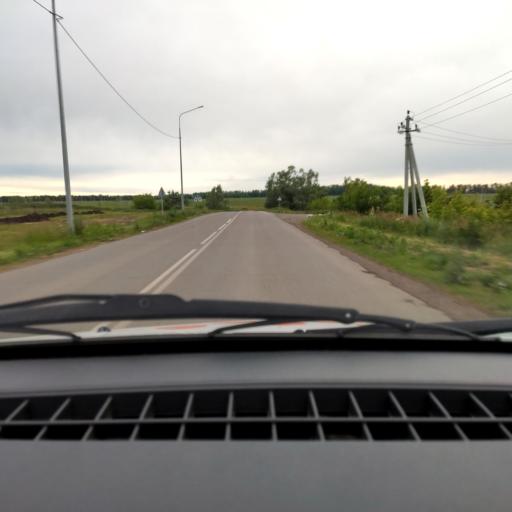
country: RU
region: Bashkortostan
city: Avdon
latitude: 54.5565
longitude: 55.7617
